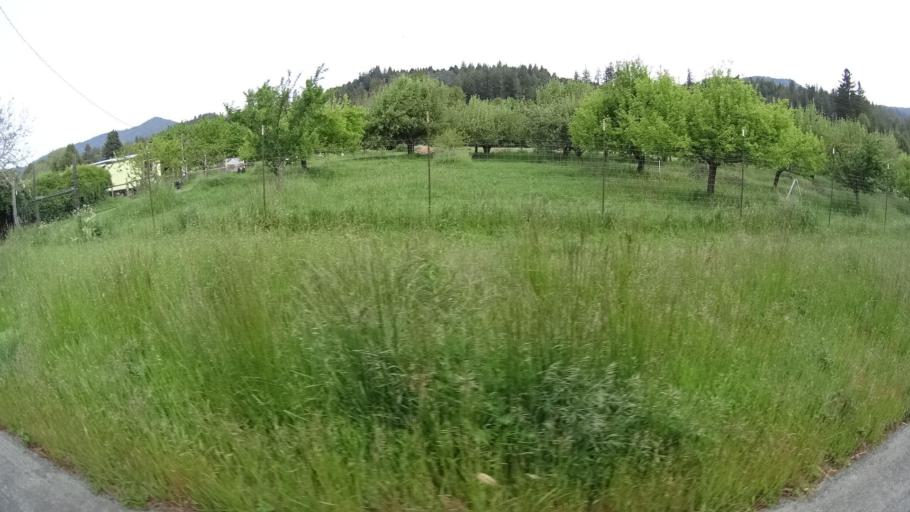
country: US
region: California
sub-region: Humboldt County
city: Redway
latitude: 40.3435
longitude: -123.8889
